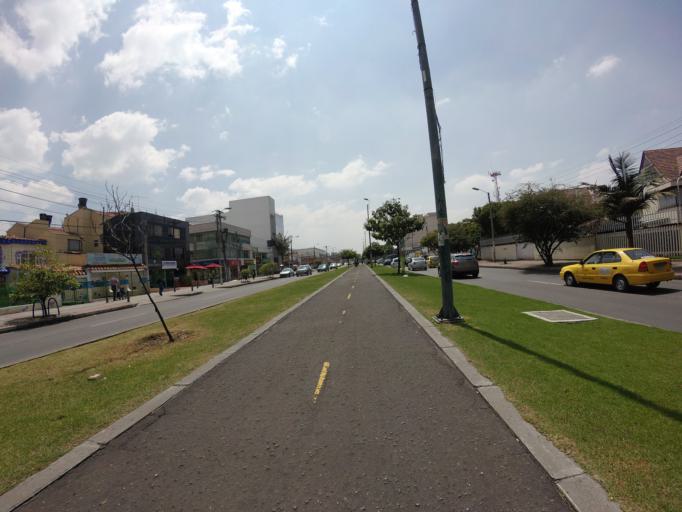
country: CO
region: Bogota D.C.
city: Barrio San Luis
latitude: 4.7252
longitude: -74.0460
